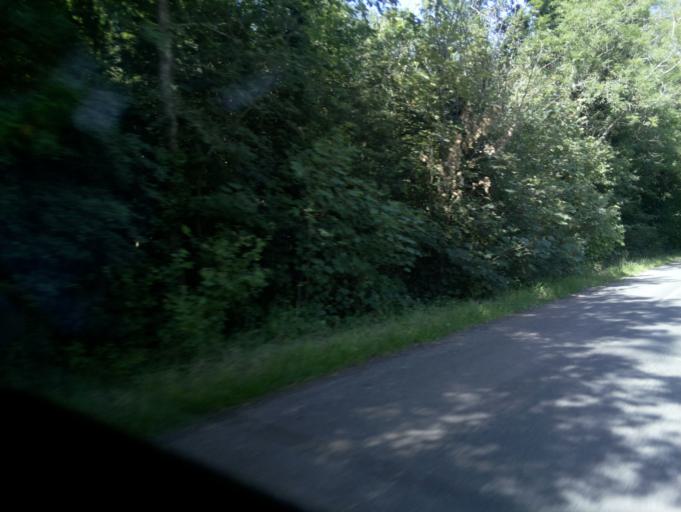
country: GB
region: England
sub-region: Buckinghamshire
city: Winslow
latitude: 51.9949
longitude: -0.8847
